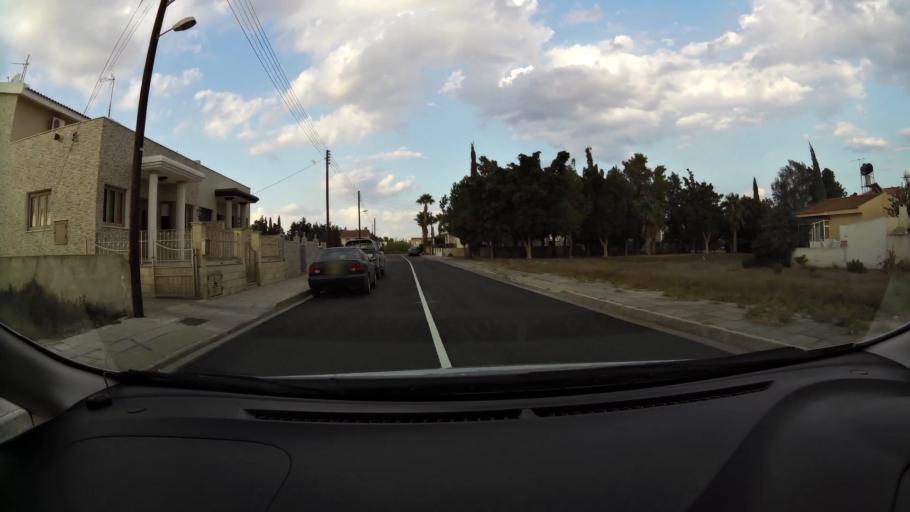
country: CY
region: Larnaka
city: Meneou
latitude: 34.8570
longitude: 33.5872
